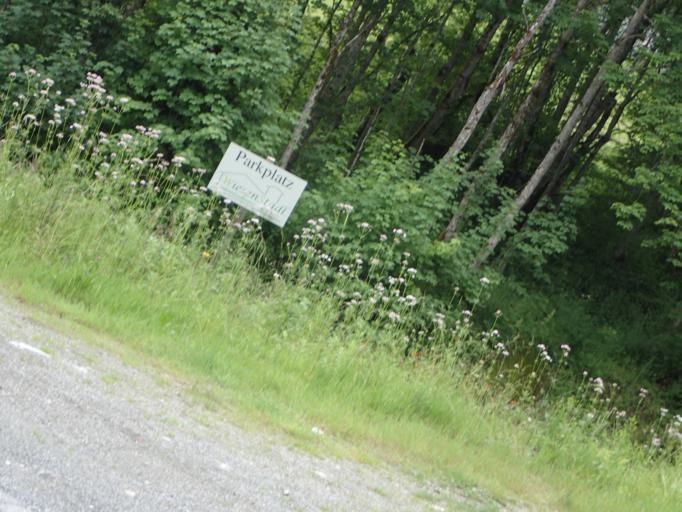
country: AT
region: Salzburg
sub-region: Politischer Bezirk Zell am See
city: Maria Alm am Steinernen Meer
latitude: 47.3836
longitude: 12.9409
